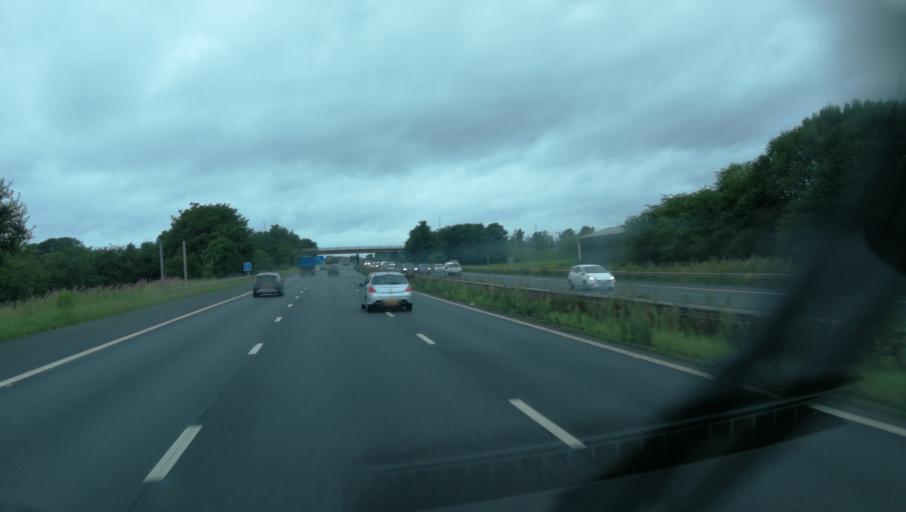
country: GB
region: England
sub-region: Borough of Bolton
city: Westhoughton
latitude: 53.5644
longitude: -2.5208
